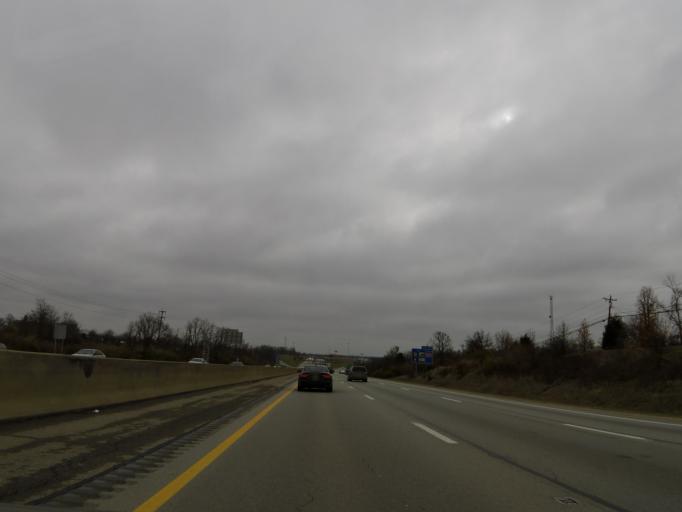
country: US
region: Kentucky
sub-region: Boone County
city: Walton
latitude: 38.8673
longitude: -84.6240
